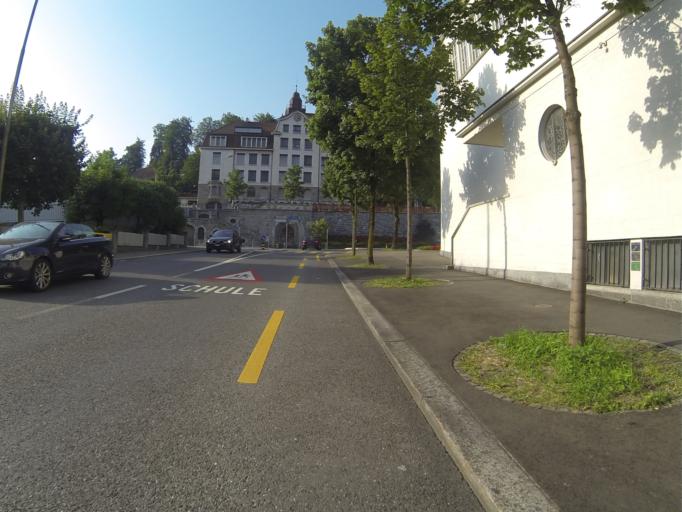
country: CH
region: Lucerne
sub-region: Lucerne-Stadt District
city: Luzern
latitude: 47.0556
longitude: 8.2921
